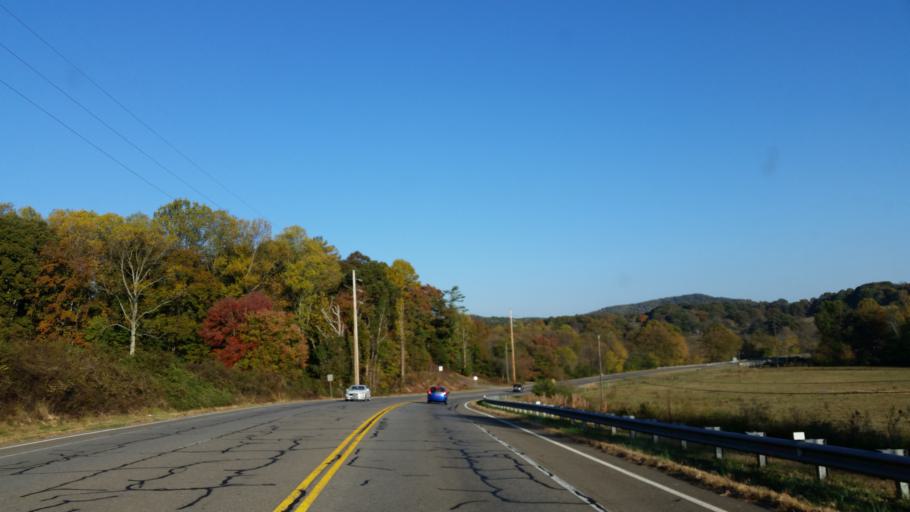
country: US
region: Georgia
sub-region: Gilmer County
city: Ellijay
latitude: 34.6511
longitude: -84.3993
